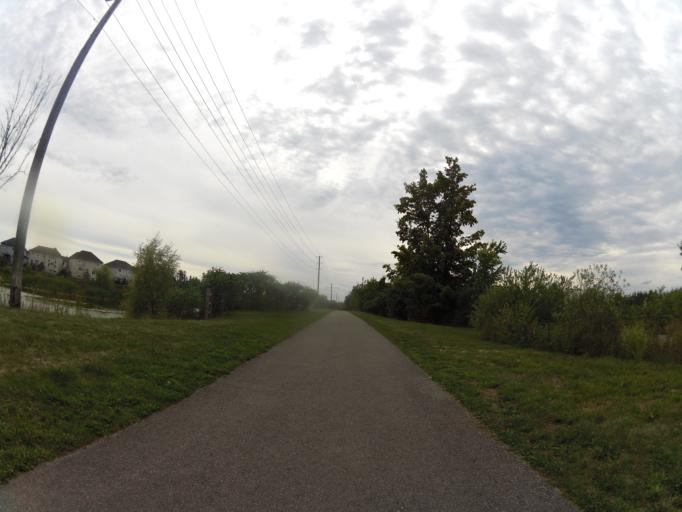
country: CA
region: Ontario
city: Bells Corners
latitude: 45.2804
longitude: -75.9337
